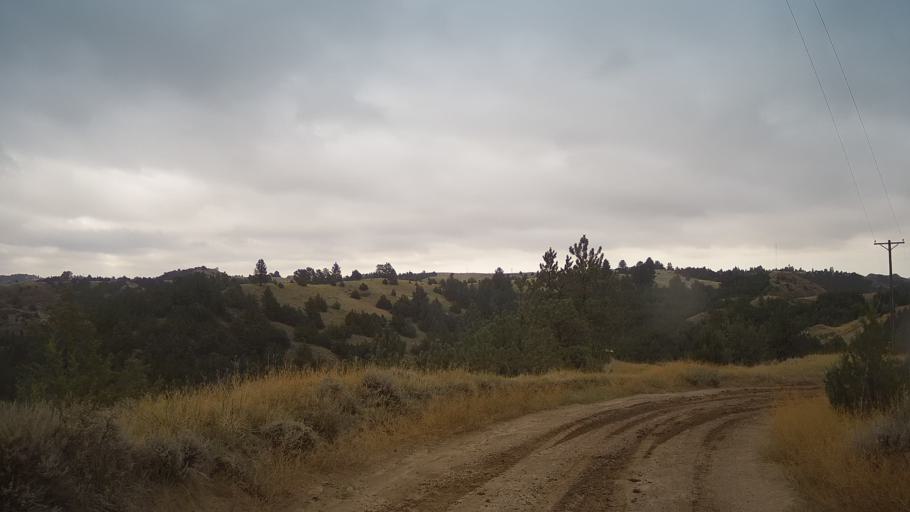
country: US
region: Montana
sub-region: Dawson County
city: Glendive
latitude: 47.0421
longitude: -104.6725
